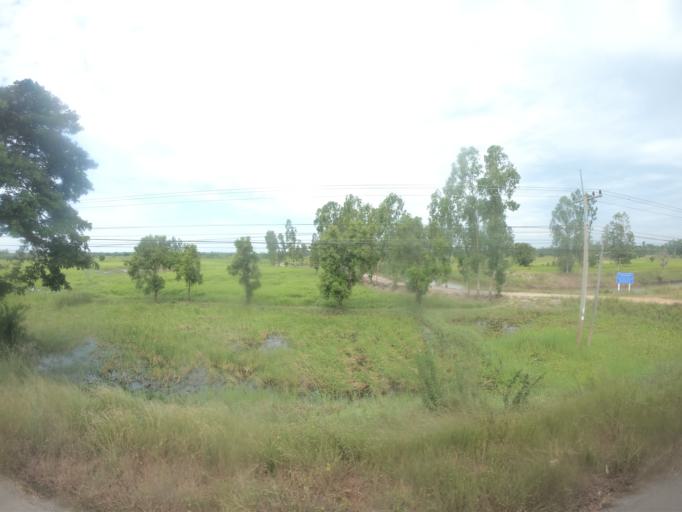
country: TH
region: Maha Sarakham
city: Chiang Yuen
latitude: 16.3366
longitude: 103.1826
